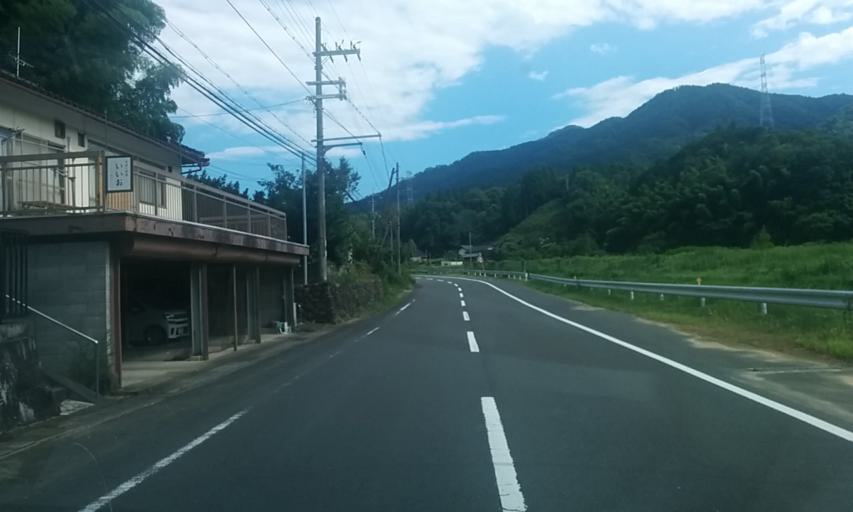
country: JP
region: Kyoto
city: Fukuchiyama
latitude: 35.3651
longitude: 135.1319
